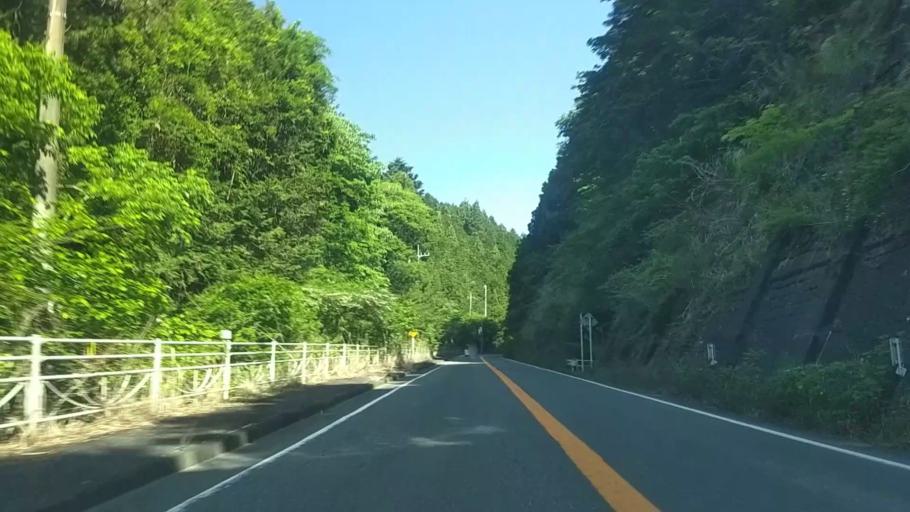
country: JP
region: Shizuoka
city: Fujinomiya
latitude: 35.2029
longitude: 138.5176
